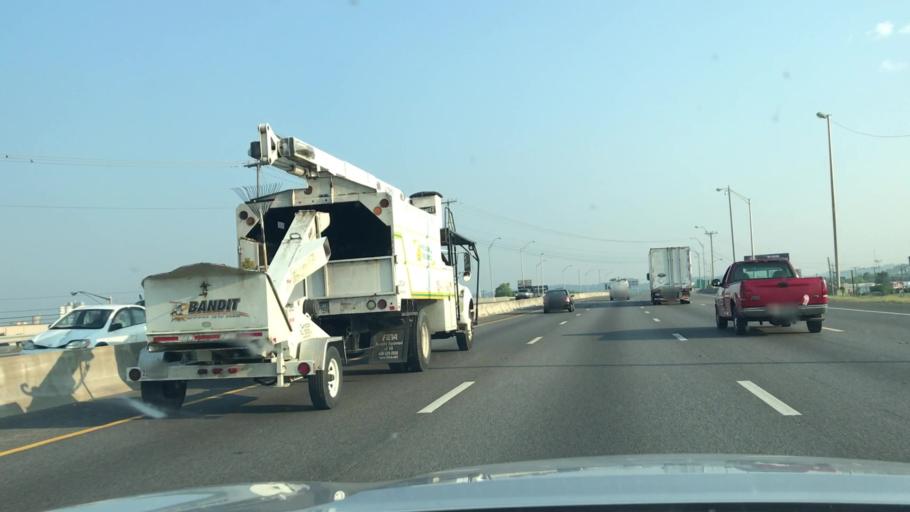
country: US
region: Tennessee
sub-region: Davidson County
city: Nashville
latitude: 36.1810
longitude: -86.7737
